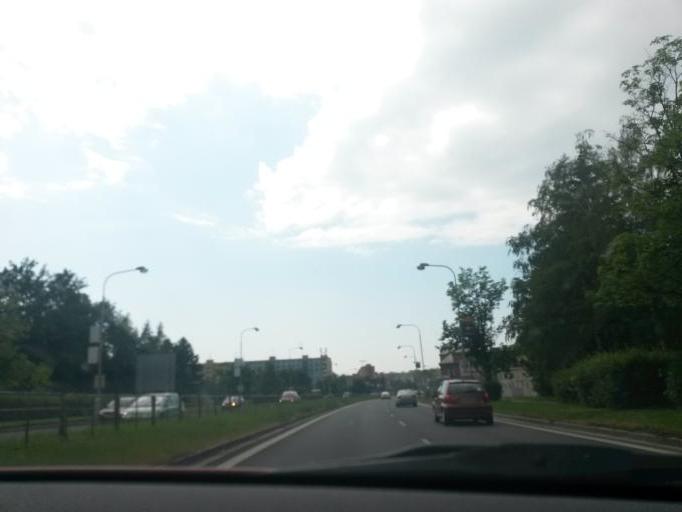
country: CZ
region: Olomoucky
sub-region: Okres Olomouc
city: Olomouc
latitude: 49.5810
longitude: 17.2530
